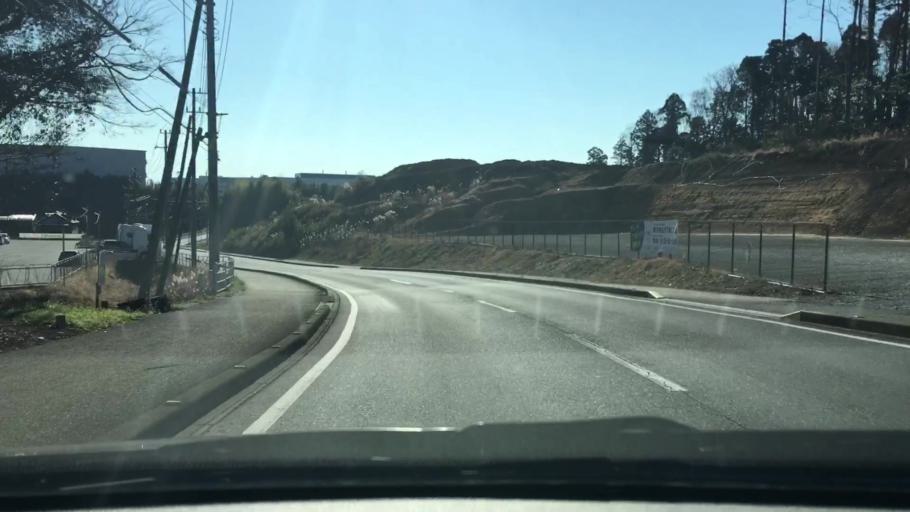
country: JP
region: Chiba
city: Shisui
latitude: 35.7201
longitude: 140.3248
